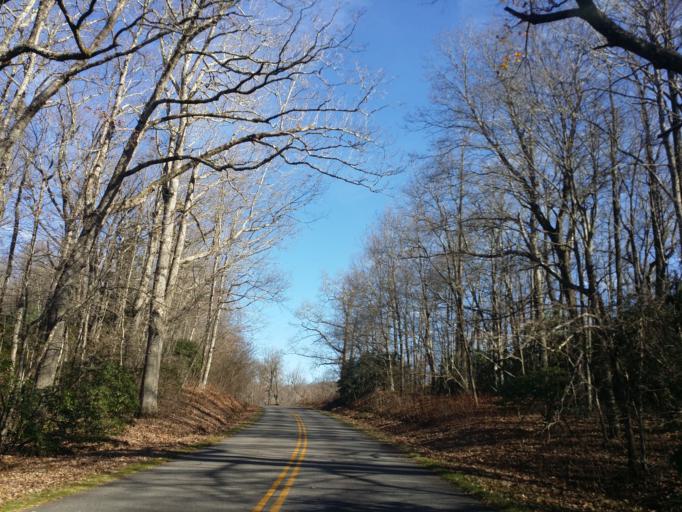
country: US
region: North Carolina
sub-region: Mitchell County
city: Spruce Pine
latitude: 35.8052
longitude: -82.1480
